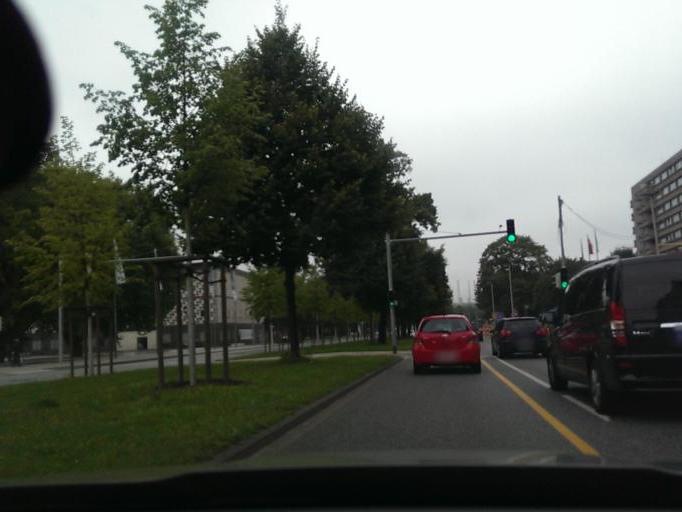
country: DE
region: Lower Saxony
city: Hannover
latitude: 52.3683
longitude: 9.7384
